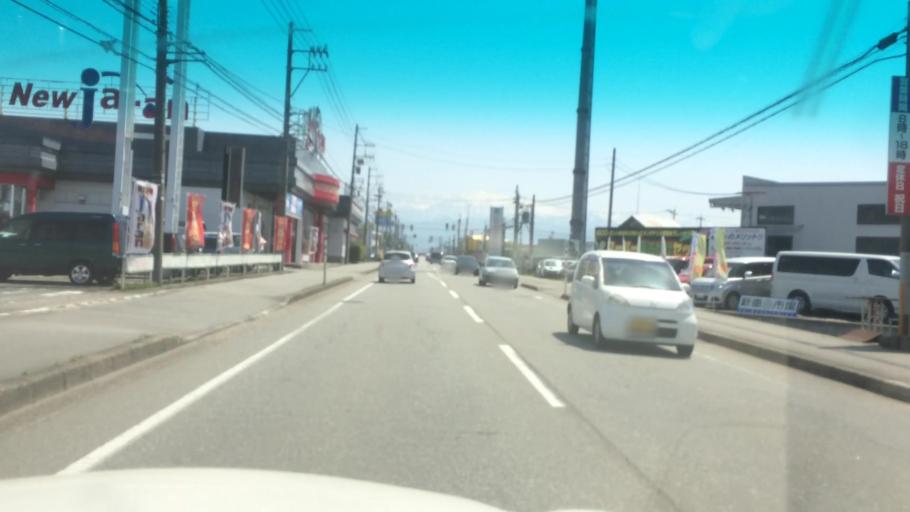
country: JP
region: Toyama
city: Toyama-shi
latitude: 36.6738
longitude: 137.2637
